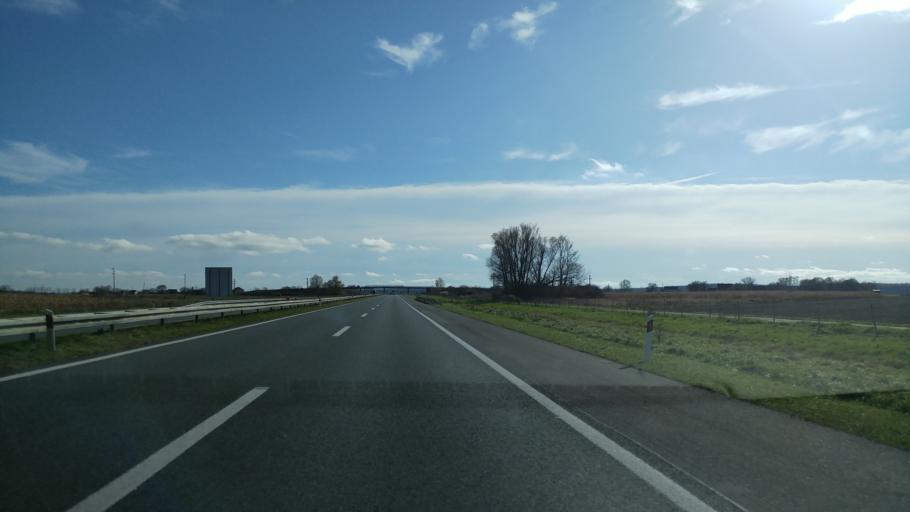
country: HR
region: Sisacko-Moslavacka
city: Lipovljani
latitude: 45.3933
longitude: 16.8652
